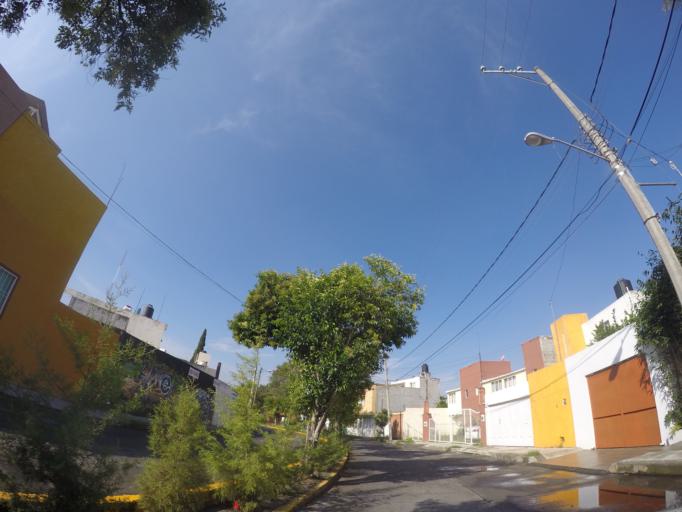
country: MX
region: Michoacan
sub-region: Morelia
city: Morelos
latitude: 19.6764
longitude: -101.2143
